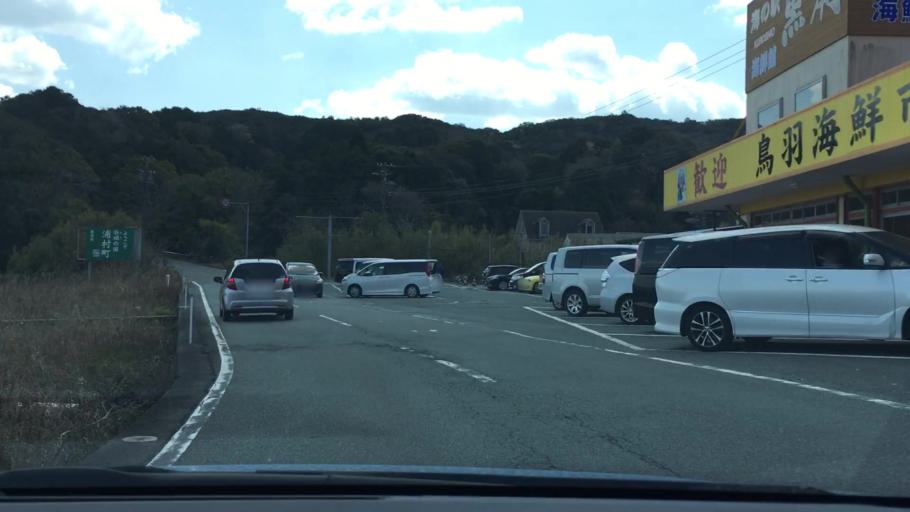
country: JP
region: Mie
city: Toba
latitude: 34.4502
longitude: 136.8750
